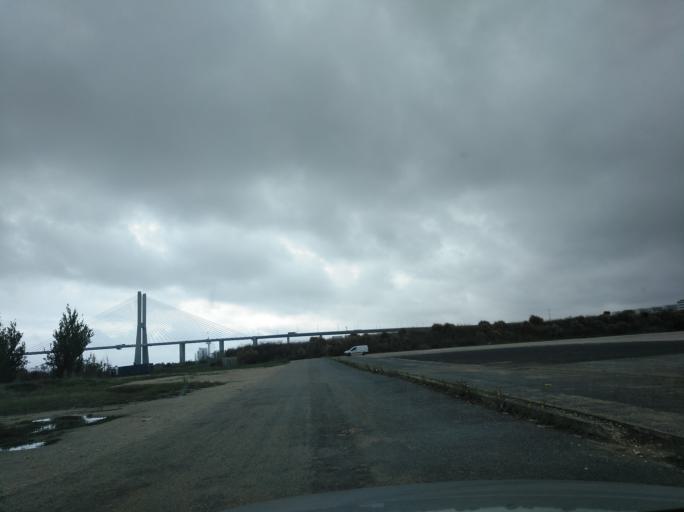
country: PT
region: Lisbon
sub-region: Loures
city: Bobadela
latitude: 38.7954
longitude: -9.0921
